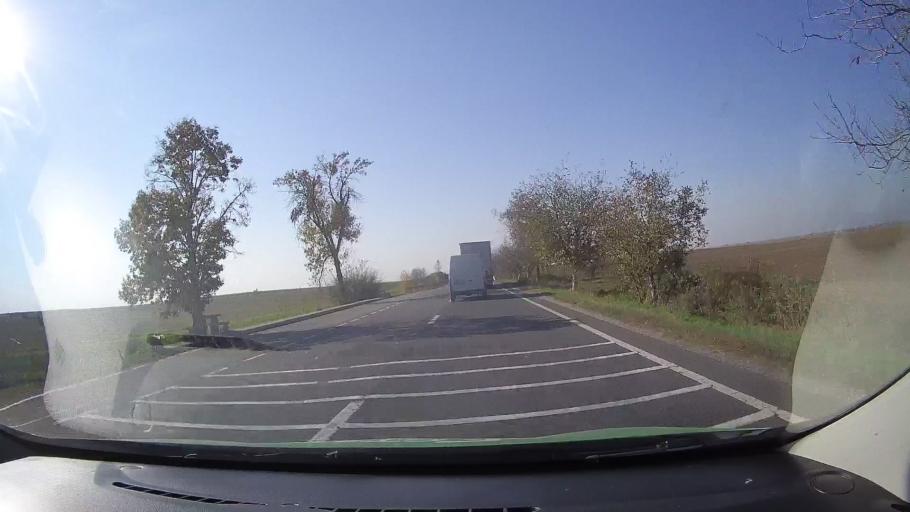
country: RO
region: Satu Mare
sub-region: Comuna Petresti
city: Petresti
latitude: 47.6369
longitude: 22.4006
